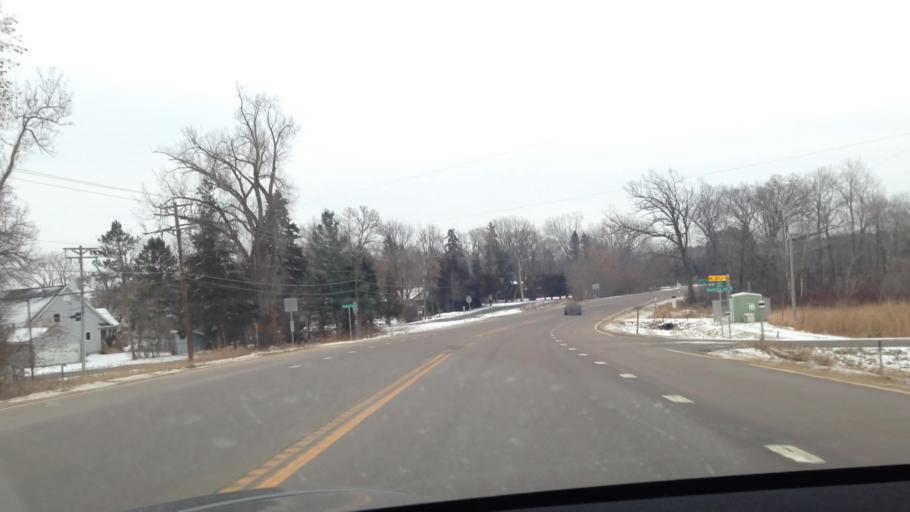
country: US
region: Minnesota
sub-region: Washington County
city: Forest Lake
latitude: 45.2625
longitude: -92.9472
